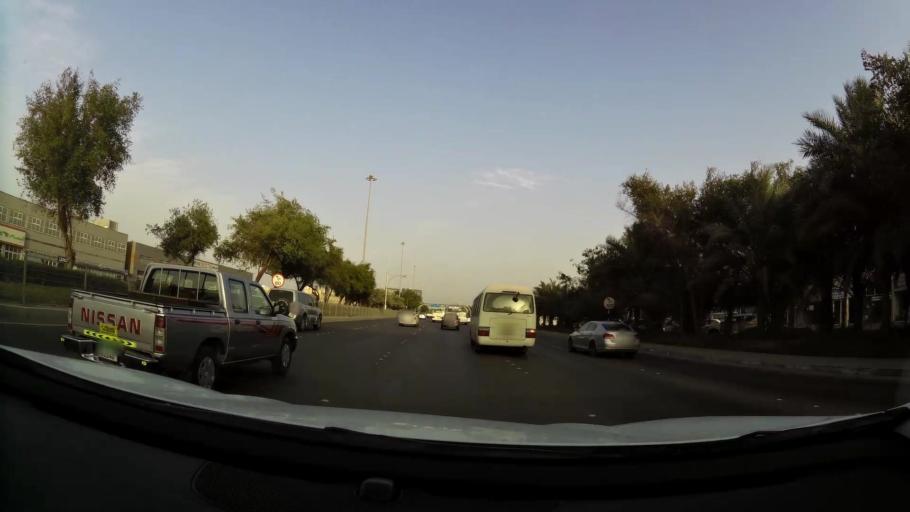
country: AE
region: Abu Dhabi
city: Abu Dhabi
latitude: 24.3733
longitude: 54.5166
